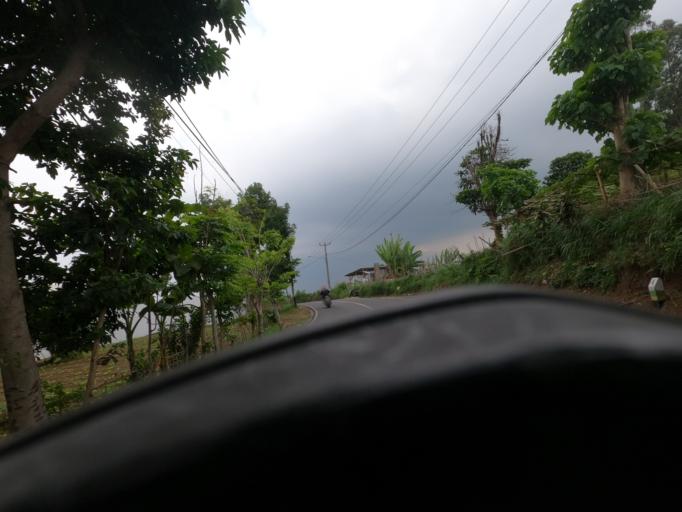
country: ID
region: West Java
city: Cimahi
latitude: -6.8162
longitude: 107.5428
